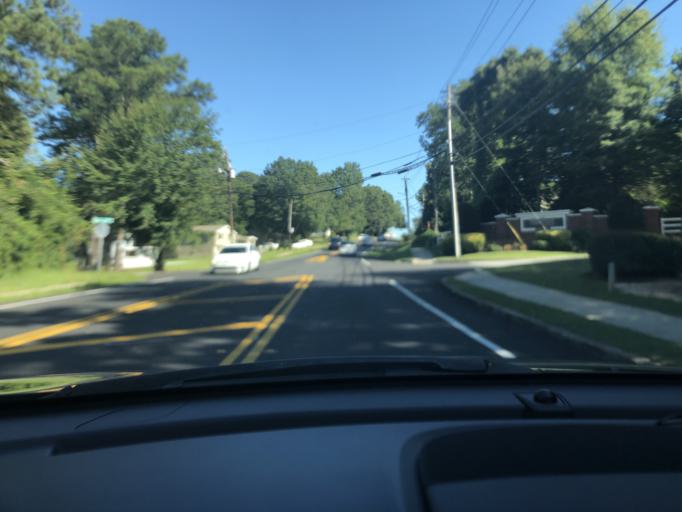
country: US
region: Georgia
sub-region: Gwinnett County
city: Lawrenceville
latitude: 33.9499
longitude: -83.9781
